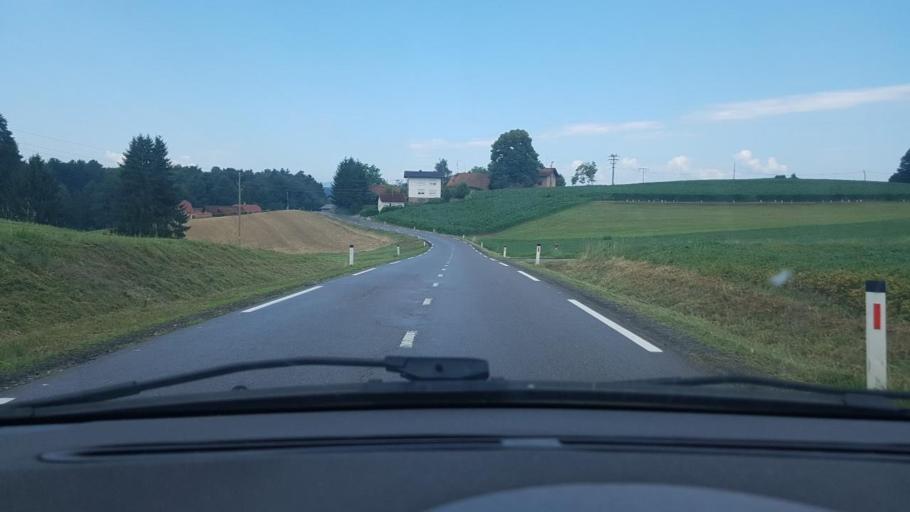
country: AT
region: Styria
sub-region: Politischer Bezirk Suedoststeiermark
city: Mureck
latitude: 46.6933
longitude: 15.7714
